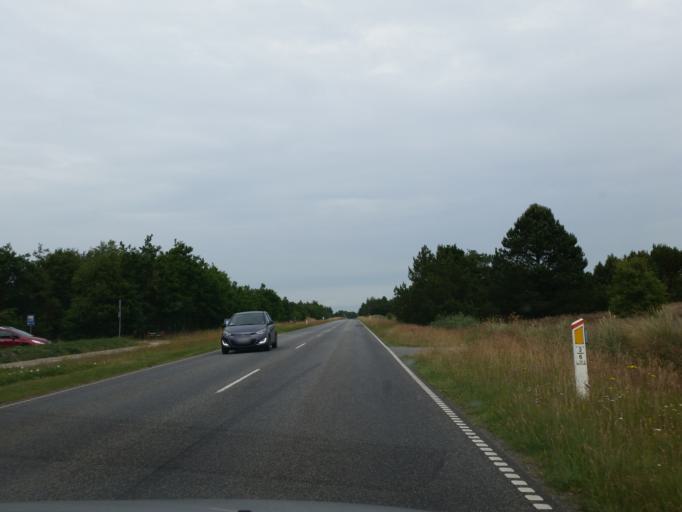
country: DE
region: Schleswig-Holstein
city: List
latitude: 55.1201
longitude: 8.5472
